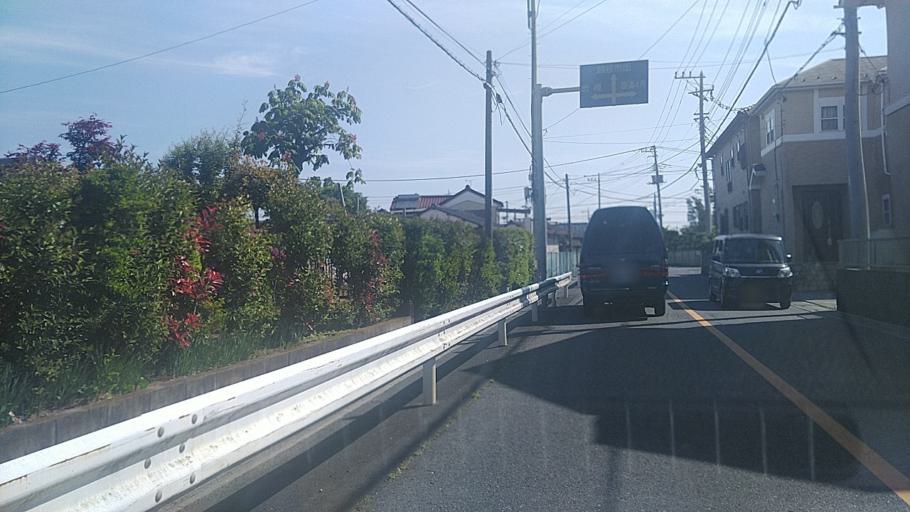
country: JP
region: Saitama
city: Koshigaya
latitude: 35.8747
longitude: 139.7603
